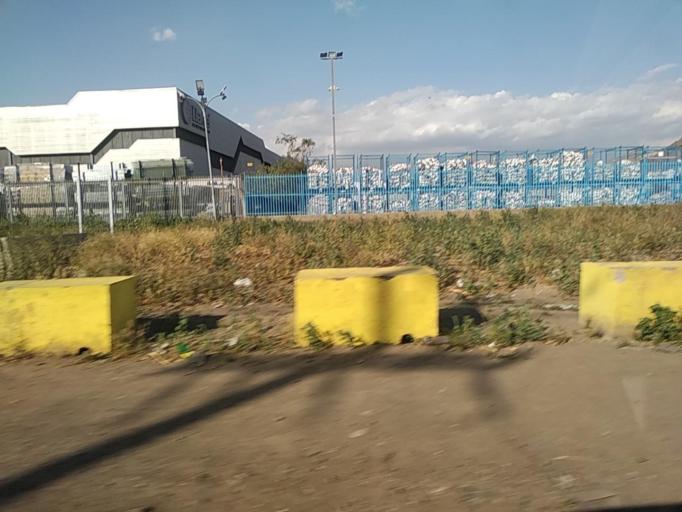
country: CL
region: Santiago Metropolitan
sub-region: Provincia de Chacabuco
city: Chicureo Abajo
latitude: -33.3083
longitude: -70.7162
